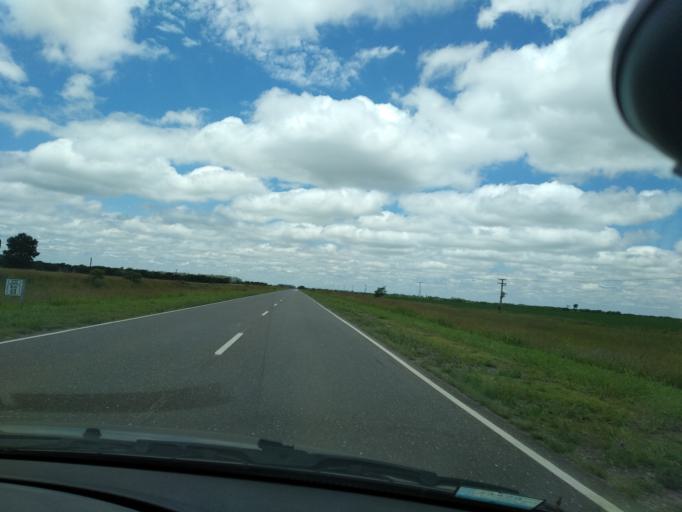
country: AR
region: Cordoba
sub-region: Departamento de Rio Segundo
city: Rio Segundo
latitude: -31.6437
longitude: -63.9725
